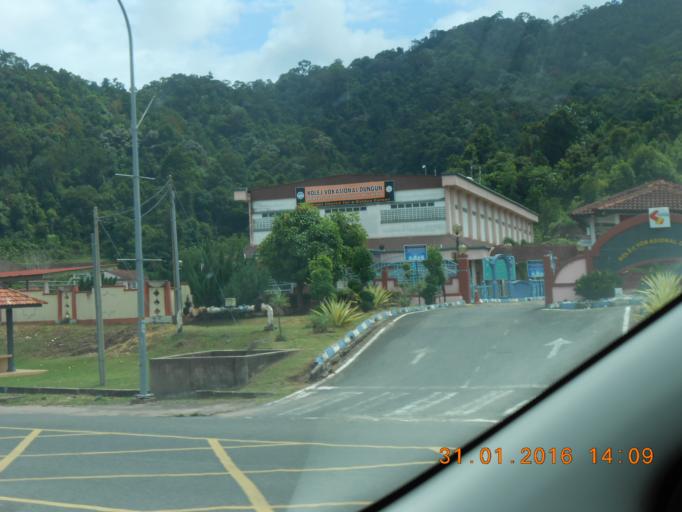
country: MY
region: Terengganu
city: Paka
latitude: 4.7134
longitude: 103.4127
